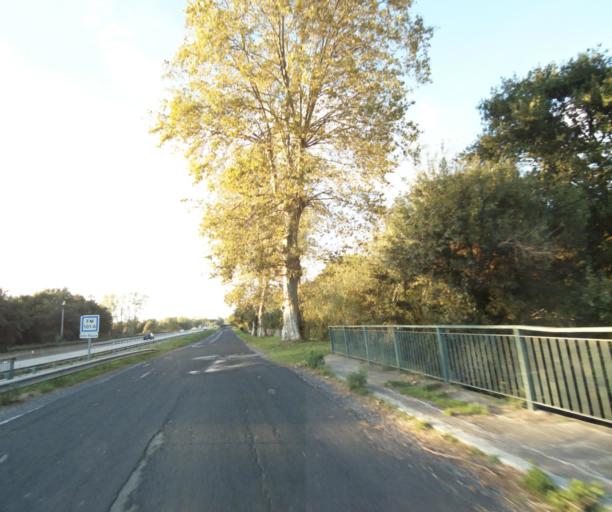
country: FR
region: Languedoc-Roussillon
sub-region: Departement des Pyrenees-Orientales
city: Argelers
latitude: 42.5693
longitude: 3.0004
